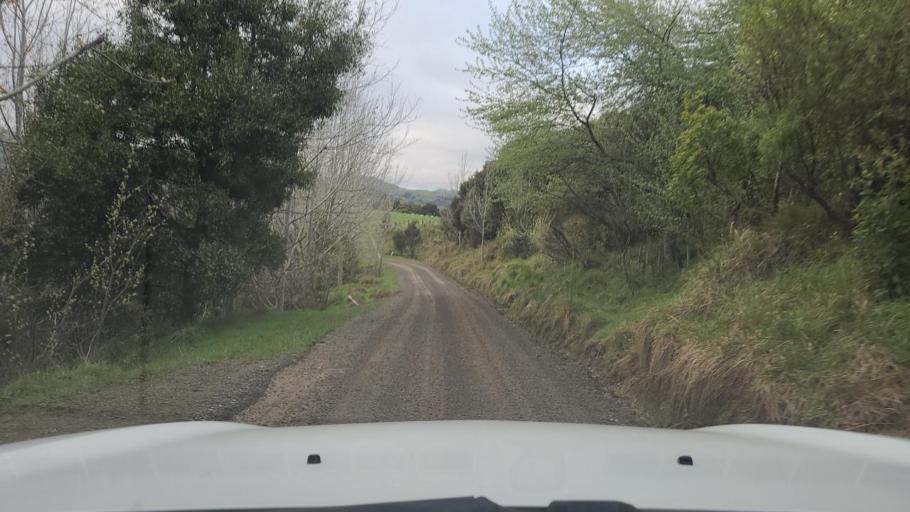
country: NZ
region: Wellington
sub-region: Masterton District
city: Masterton
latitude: -41.1623
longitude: 175.6868
